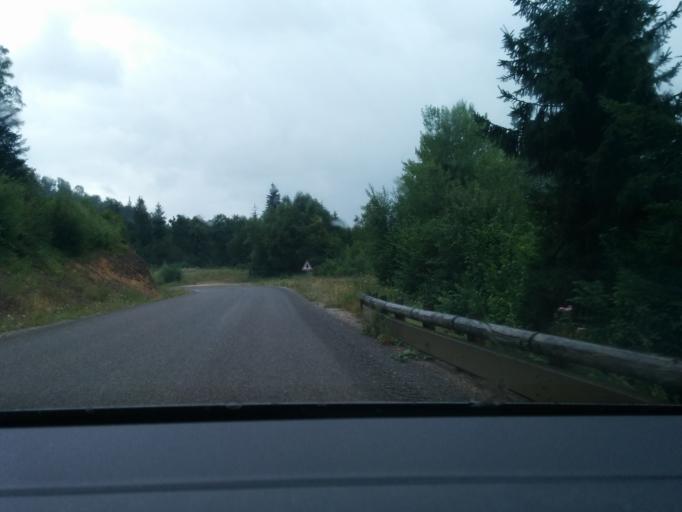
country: FR
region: Franche-Comte
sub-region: Departement du Jura
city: Saint-Lupicin
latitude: 46.4354
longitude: 5.8128
